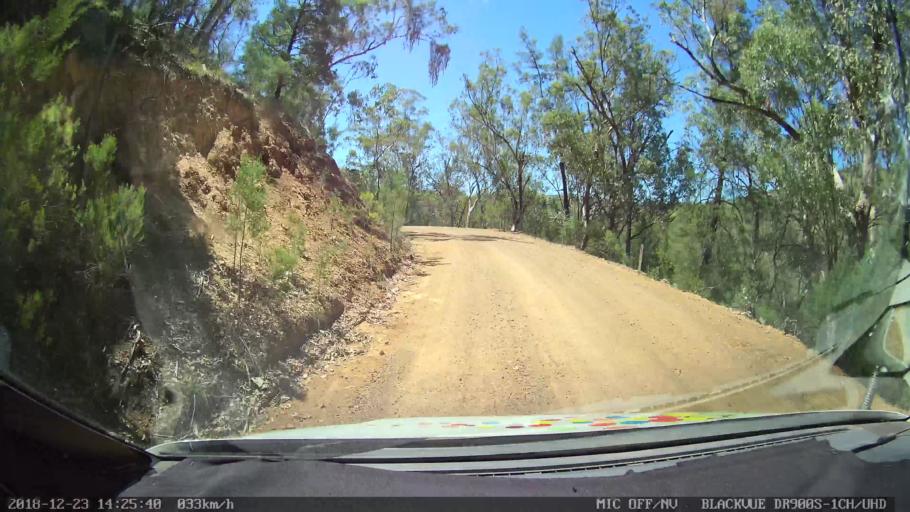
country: AU
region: New South Wales
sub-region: Tamworth Municipality
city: Manilla
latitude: -30.6260
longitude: 150.9548
